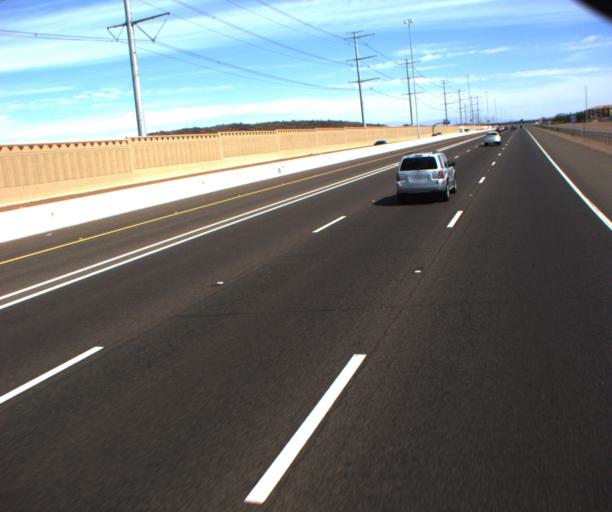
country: US
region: Arizona
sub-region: Maricopa County
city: Anthem
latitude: 33.7366
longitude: -112.1223
